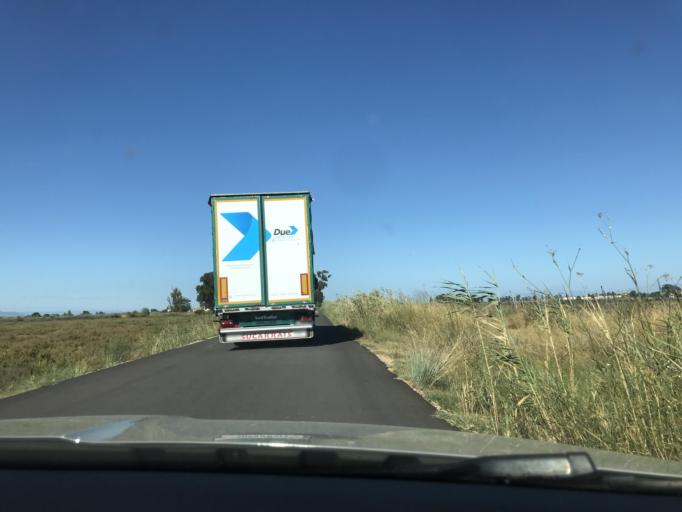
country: ES
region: Catalonia
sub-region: Provincia de Tarragona
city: Deltebre
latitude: 40.6566
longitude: 0.7725
